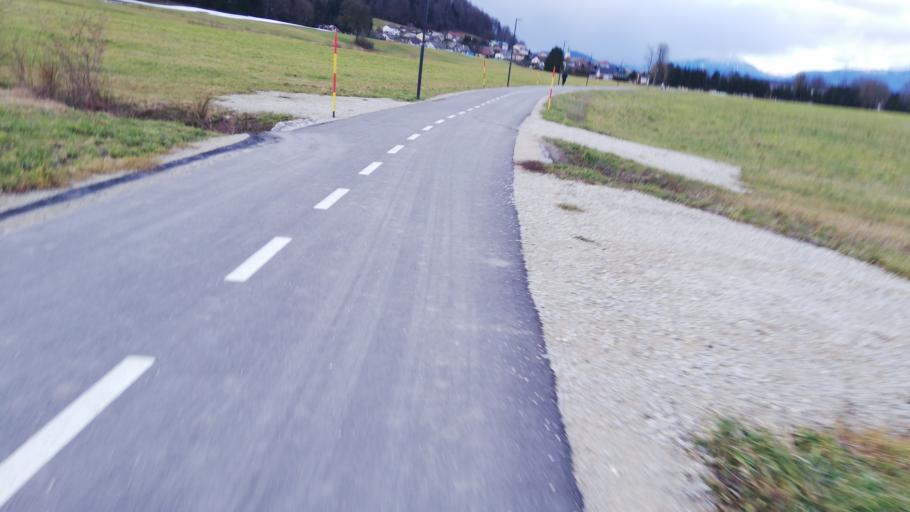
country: SI
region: Medvode
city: Medvode
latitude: 46.1259
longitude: 14.4172
